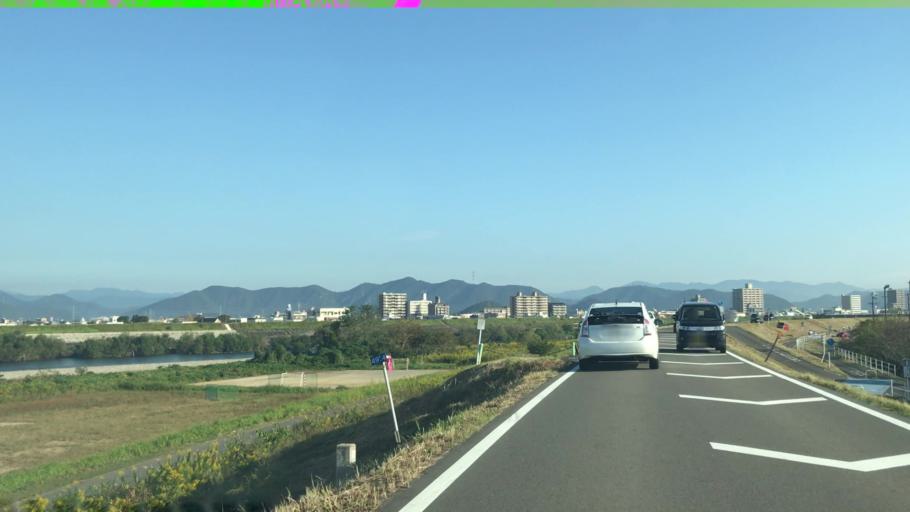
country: JP
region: Gifu
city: Gifu-shi
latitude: 35.4247
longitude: 136.7448
